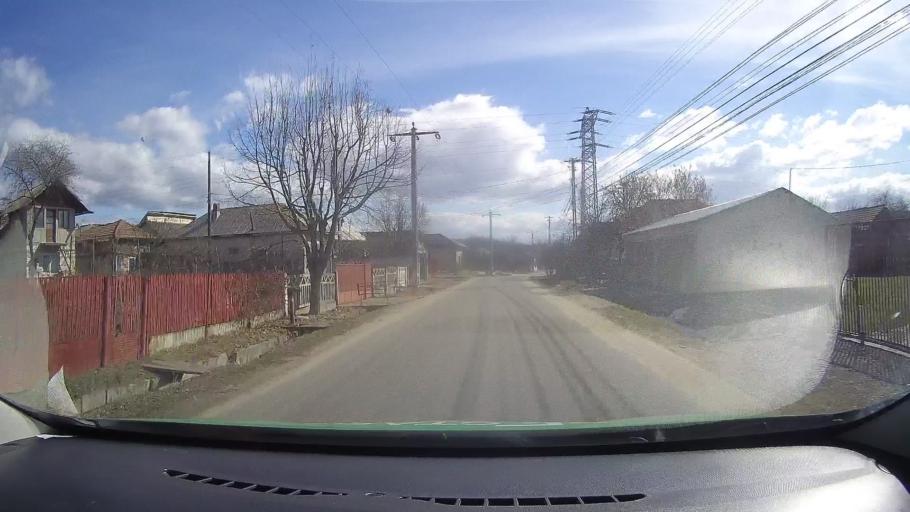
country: RO
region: Dambovita
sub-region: Comuna Branesti
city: Branesti
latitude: 45.0328
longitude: 25.4153
